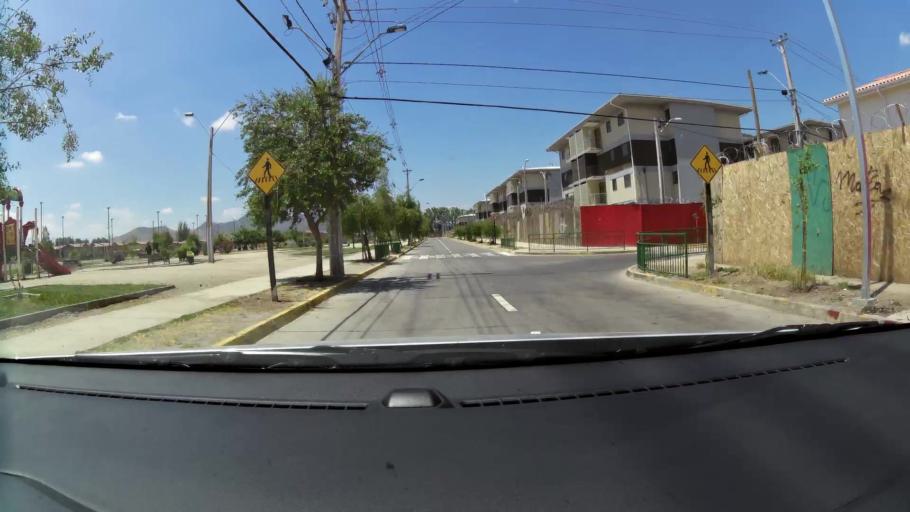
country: CL
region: Santiago Metropolitan
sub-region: Provincia de Talagante
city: Penaflor
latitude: -33.5741
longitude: -70.8026
